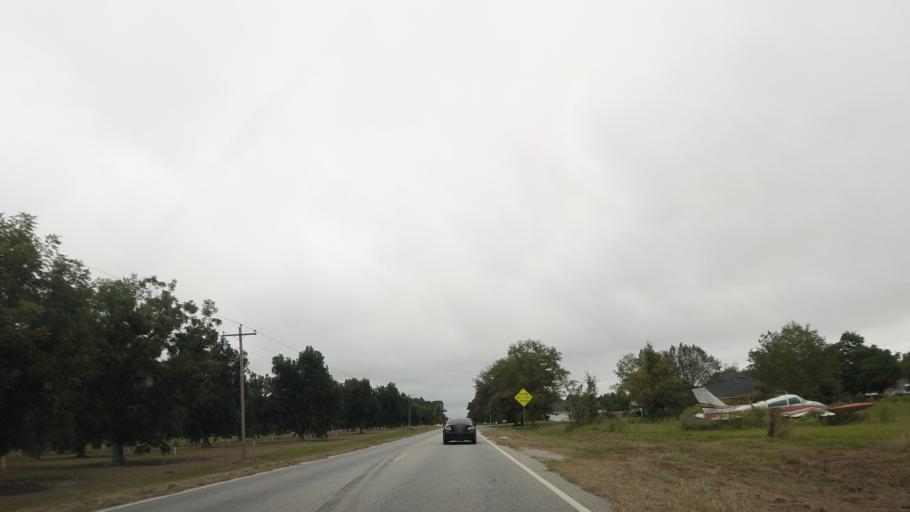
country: US
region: Georgia
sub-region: Berrien County
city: Ray City
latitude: 31.0338
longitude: -83.1978
